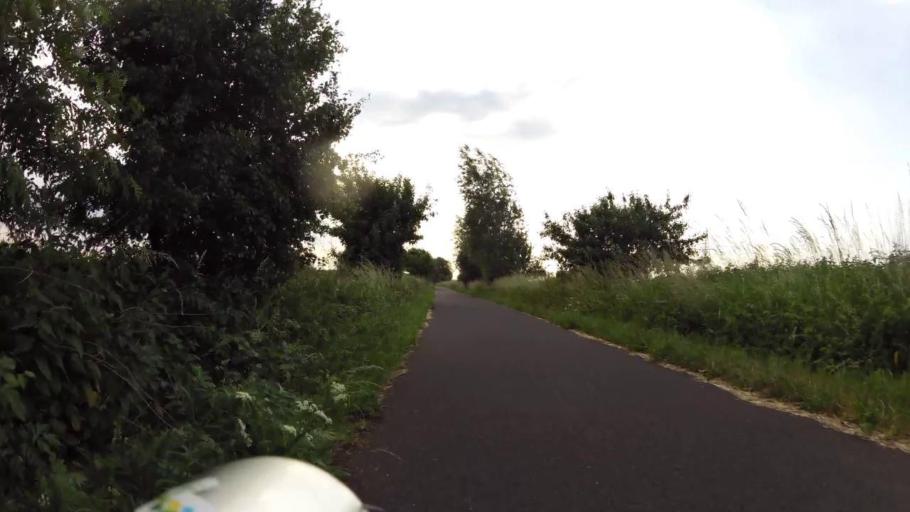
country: PL
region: Kujawsko-Pomorskie
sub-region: Powiat chelminski
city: Unislaw
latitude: 53.1803
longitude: 18.4054
